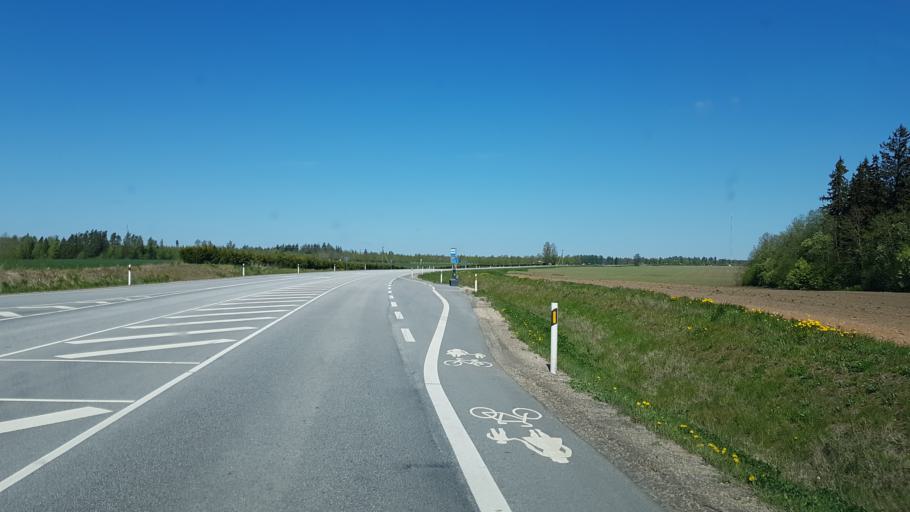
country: EE
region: Viljandimaa
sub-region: Viiratsi vald
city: Viiratsi
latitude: 58.3398
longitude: 25.6298
